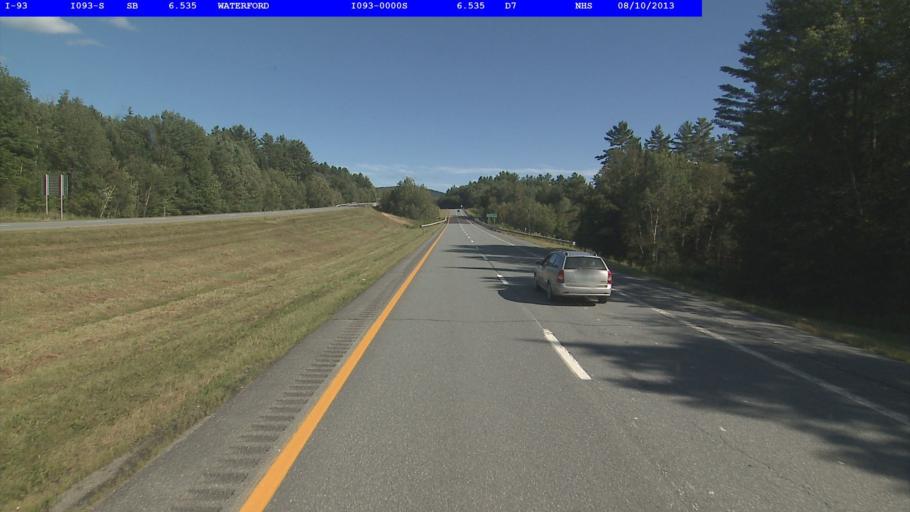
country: US
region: Vermont
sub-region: Caledonia County
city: St Johnsbury
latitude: 44.4242
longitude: -71.9388
